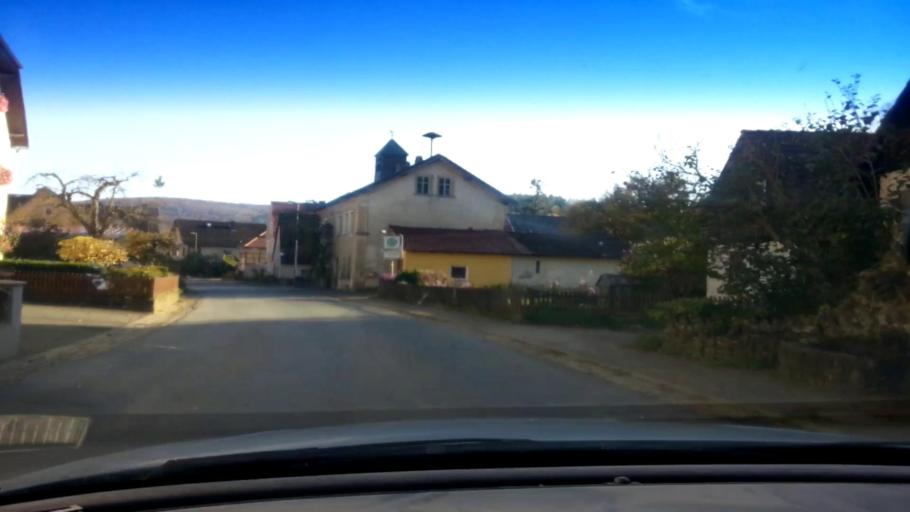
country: DE
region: Bavaria
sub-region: Upper Franconia
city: Heiligenstadt
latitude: 49.8839
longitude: 11.1282
